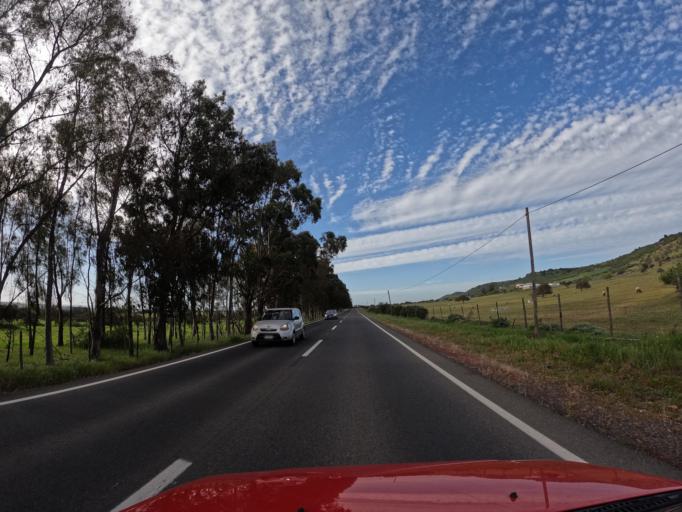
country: CL
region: O'Higgins
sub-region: Provincia de Colchagua
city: Santa Cruz
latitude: -34.1863
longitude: -71.7336
